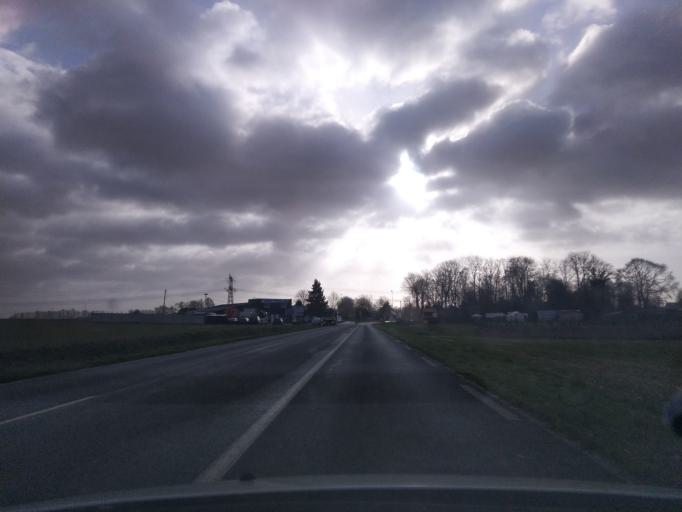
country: FR
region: Haute-Normandie
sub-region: Departement de la Seine-Maritime
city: Pissy-Poville
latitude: 49.5212
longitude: 0.9867
